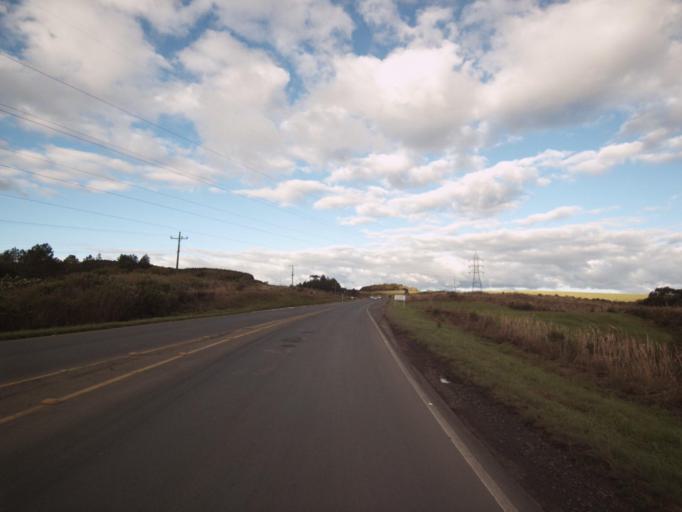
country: BR
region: Santa Catarina
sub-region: Campos Novos
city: Campos Novos
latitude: -27.3938
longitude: -51.1911
